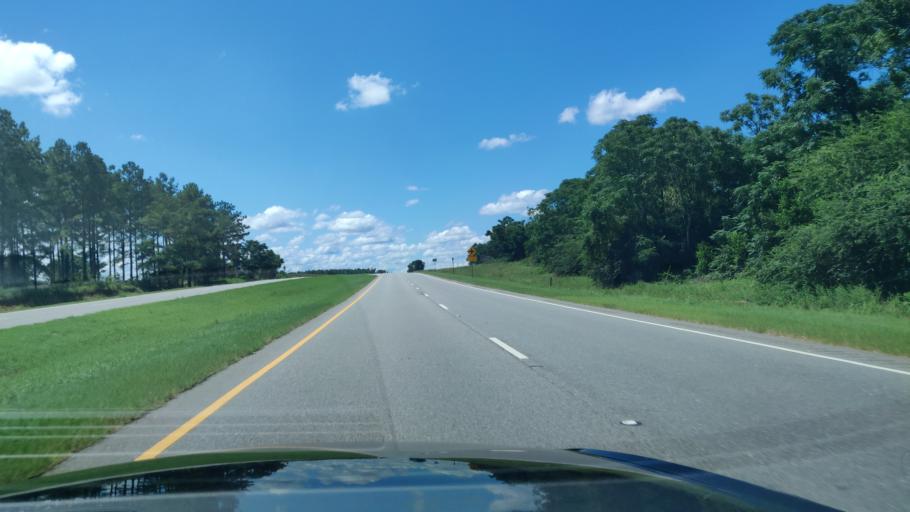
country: US
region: Georgia
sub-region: Terrell County
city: Dawson
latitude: 31.8530
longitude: -84.4766
